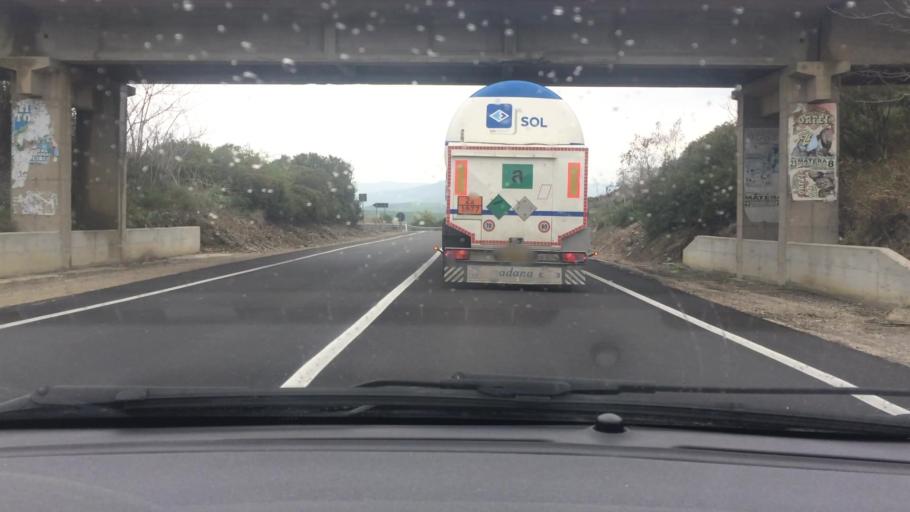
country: IT
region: Basilicate
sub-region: Provincia di Matera
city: Matera
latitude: 40.6215
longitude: 16.5844
